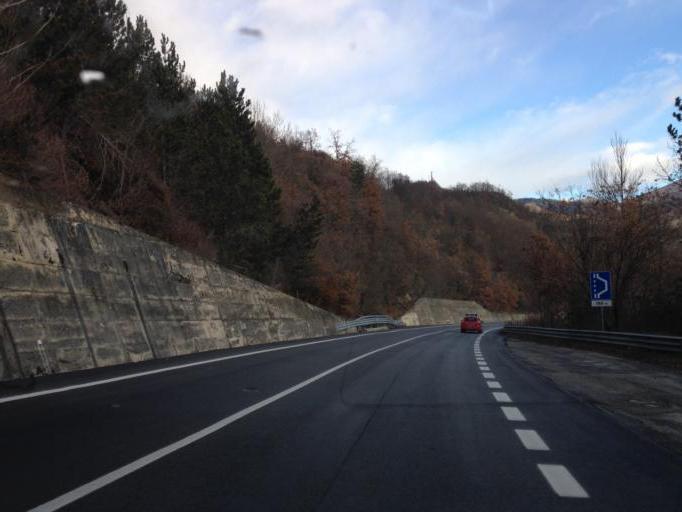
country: IT
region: The Marches
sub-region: Provincia di Ascoli Piceno
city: Arquata del Tronto
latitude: 42.7639
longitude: 13.2847
